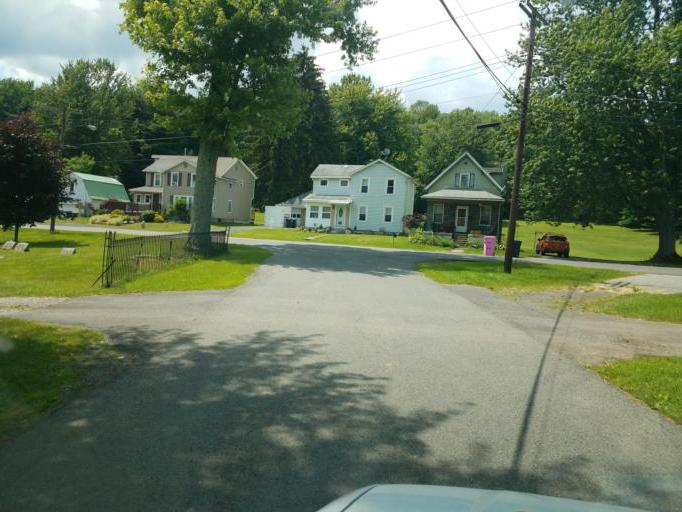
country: US
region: New York
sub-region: Wayne County
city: Clyde
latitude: 43.0770
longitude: -76.8682
